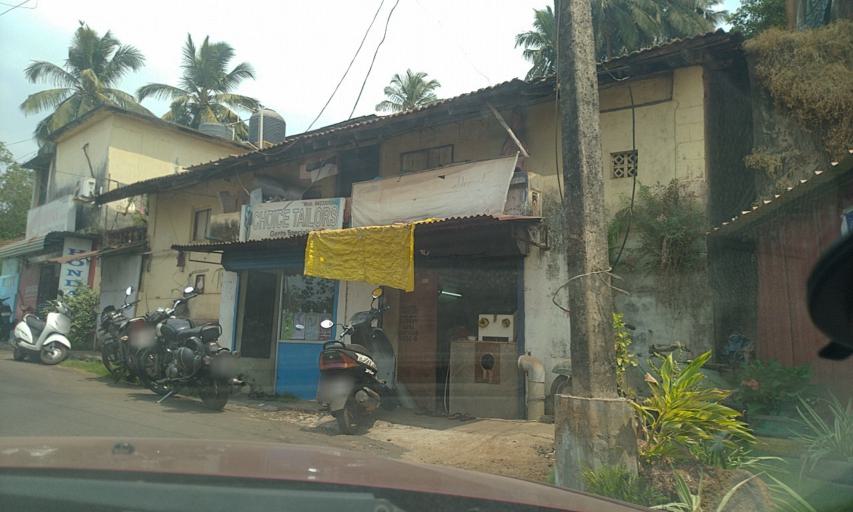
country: IN
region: Goa
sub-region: North Goa
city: Mapuca
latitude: 15.5923
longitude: 73.8107
